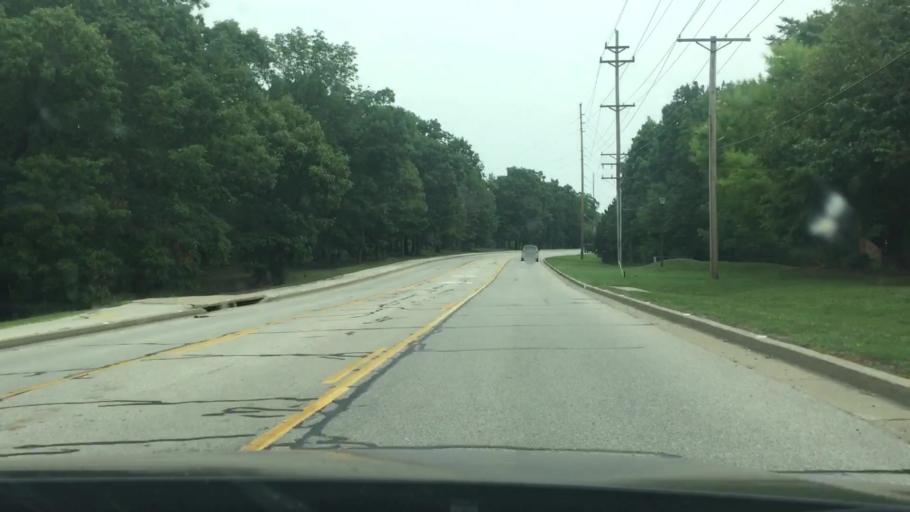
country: US
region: Missouri
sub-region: Camden County
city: Four Seasons
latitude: 38.1905
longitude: -92.6953
